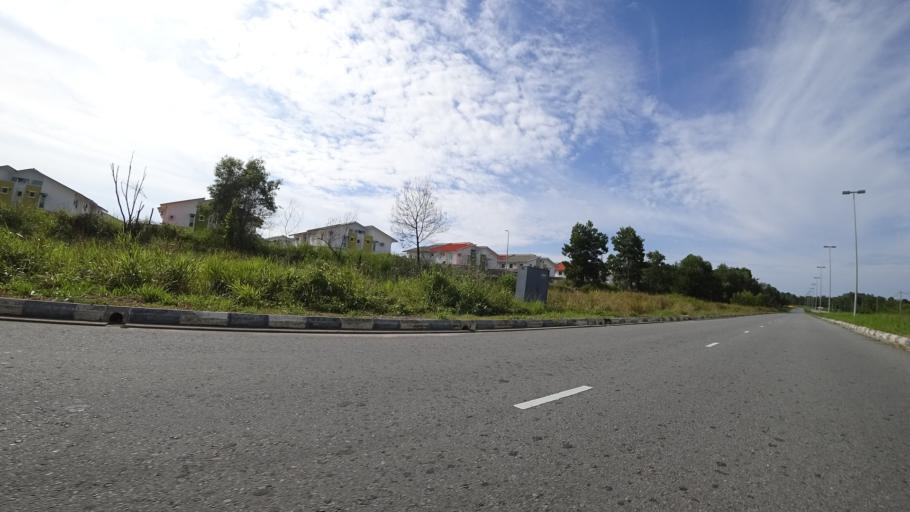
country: BN
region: Brunei and Muara
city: Bandar Seri Begawan
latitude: 4.8930
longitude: 114.8035
